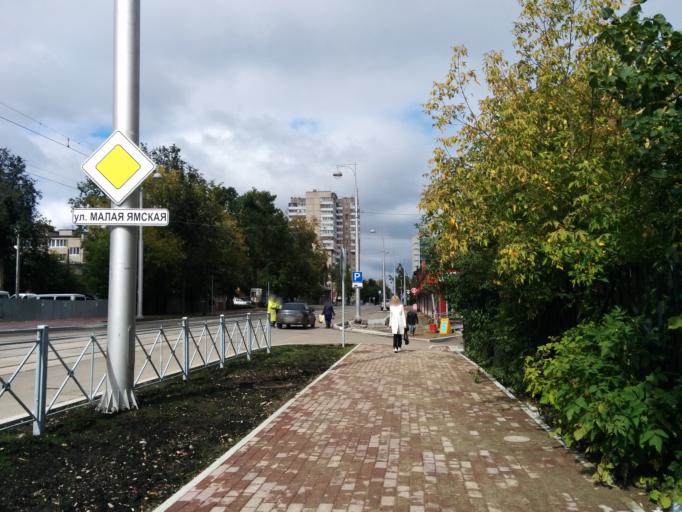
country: RU
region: Perm
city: Perm
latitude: 58.0087
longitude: 56.2589
